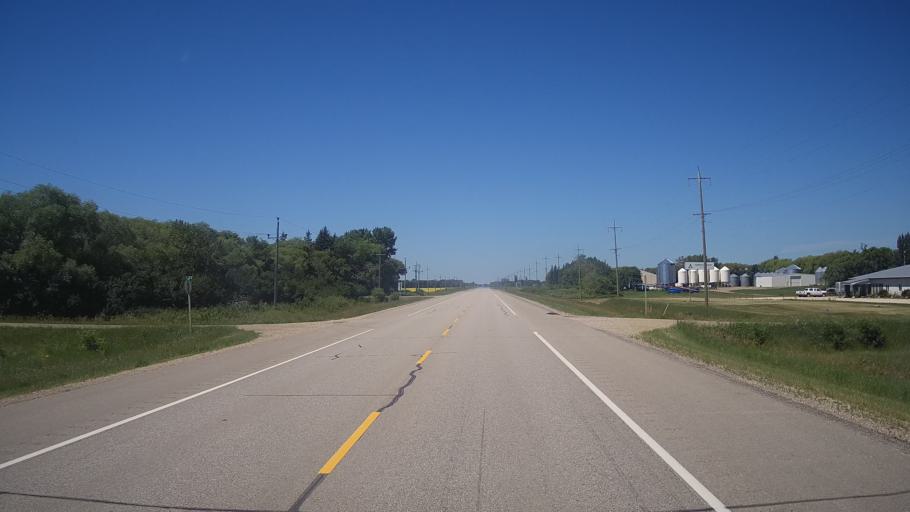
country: CA
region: Manitoba
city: Neepawa
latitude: 50.2252
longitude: -99.3159
